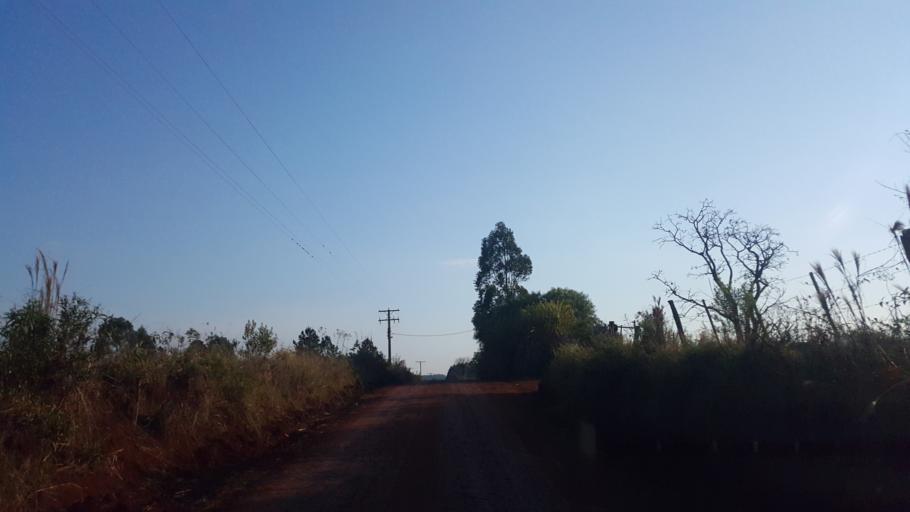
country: AR
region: Misiones
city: Capiovi
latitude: -26.9077
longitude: -55.0507
